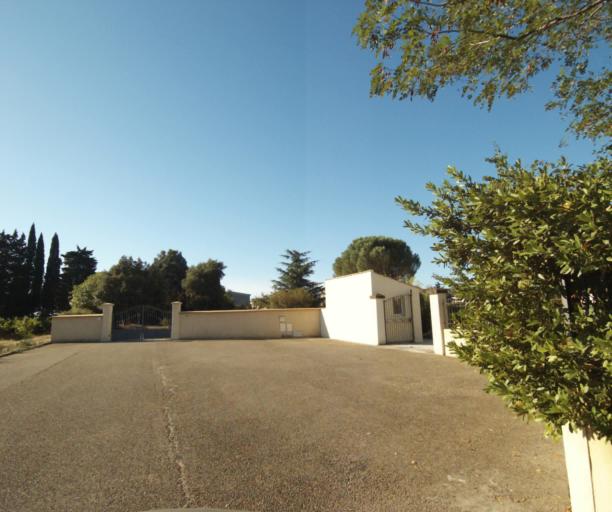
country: FR
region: Languedoc-Roussillon
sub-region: Departement du Gard
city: Bouillargues
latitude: 43.7931
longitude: 4.4391
